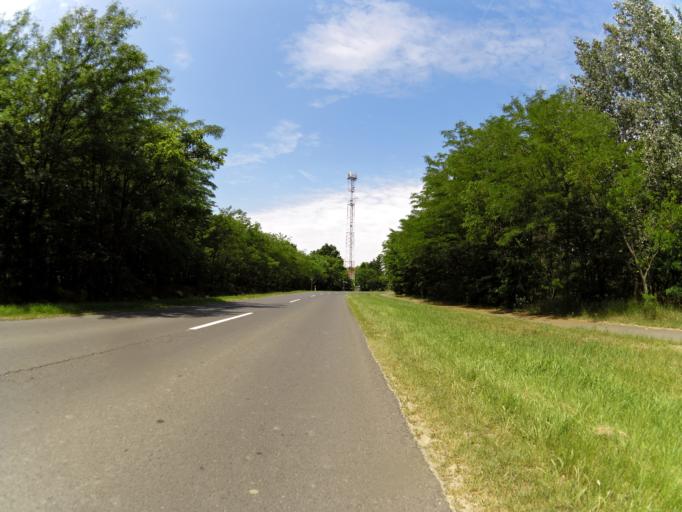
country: HU
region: Csongrad
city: Opusztaszer
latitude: 46.4880
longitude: 20.0764
